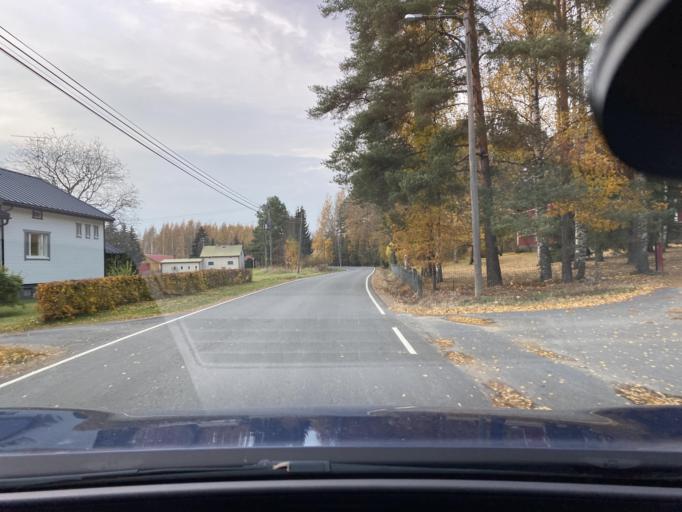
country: FI
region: Varsinais-Suomi
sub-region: Loimaa
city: Alastaro
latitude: 61.0871
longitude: 22.9151
